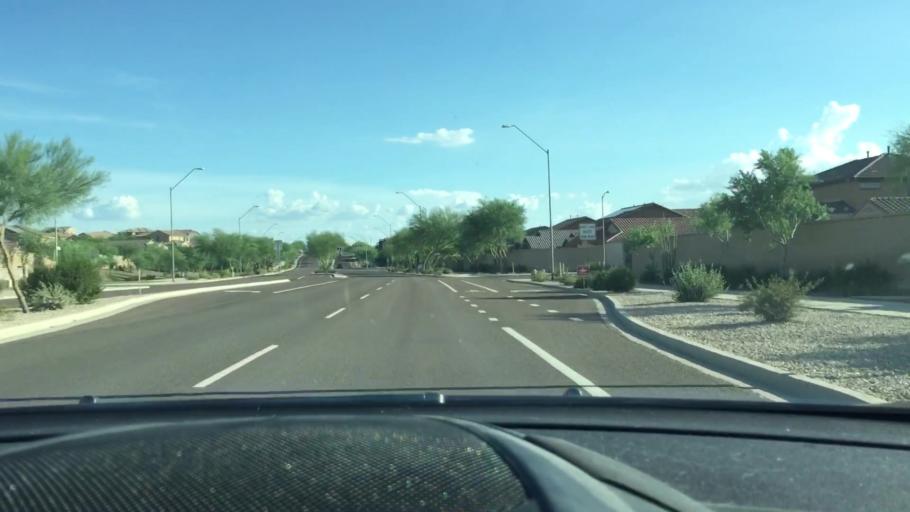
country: US
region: Arizona
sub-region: Maricopa County
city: Sun City West
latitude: 33.7194
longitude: -112.2853
